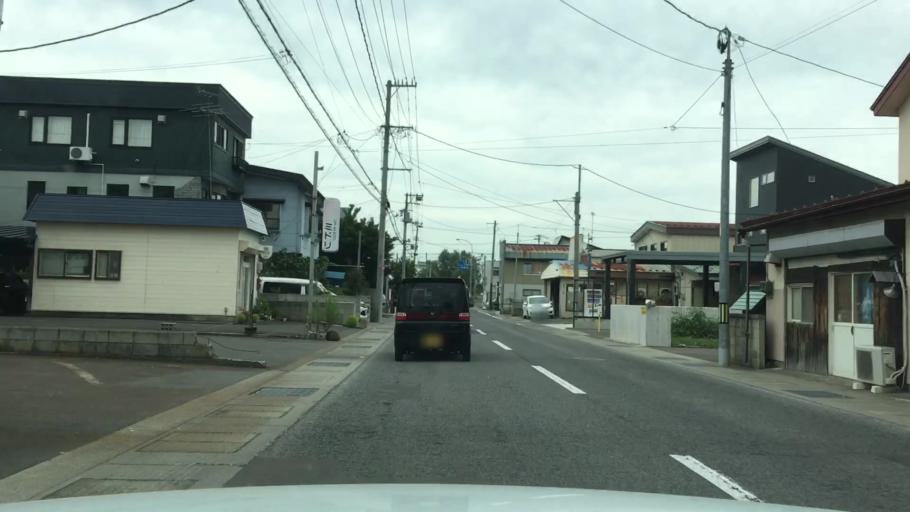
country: JP
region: Aomori
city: Hirosaki
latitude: 40.6133
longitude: 140.4619
